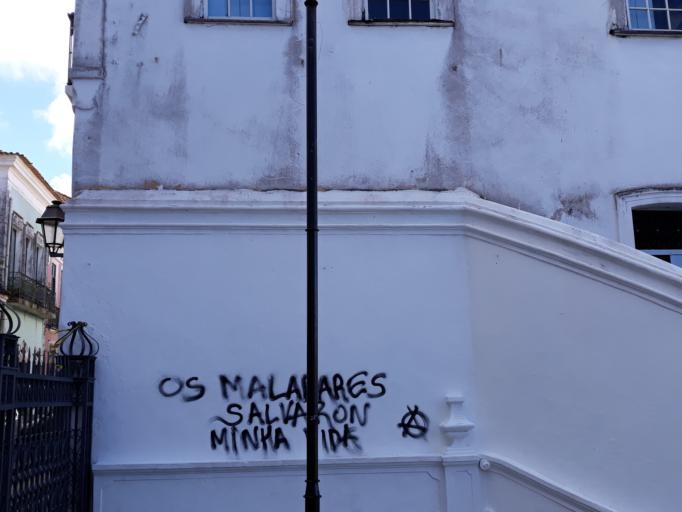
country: BR
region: Bahia
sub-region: Salvador
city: Salvador
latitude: -12.9697
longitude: -38.5081
